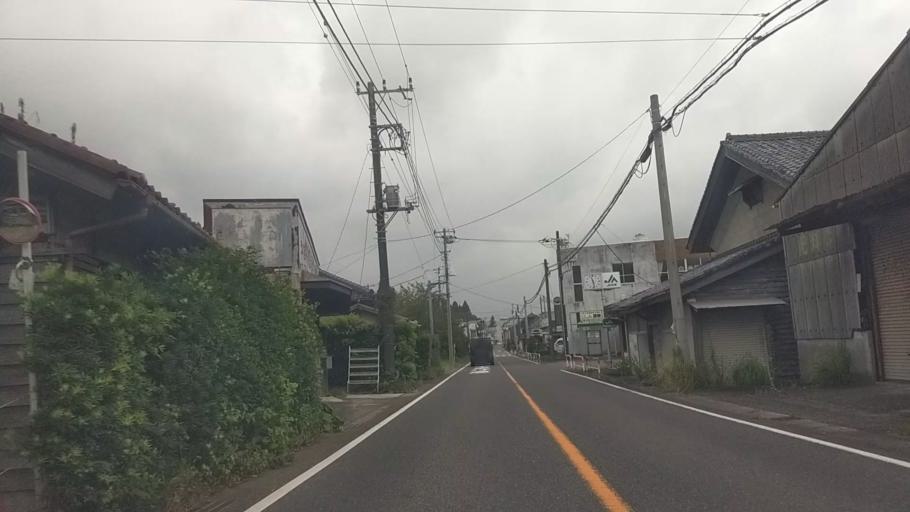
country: JP
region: Chiba
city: Kawaguchi
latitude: 35.1317
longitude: 140.0106
